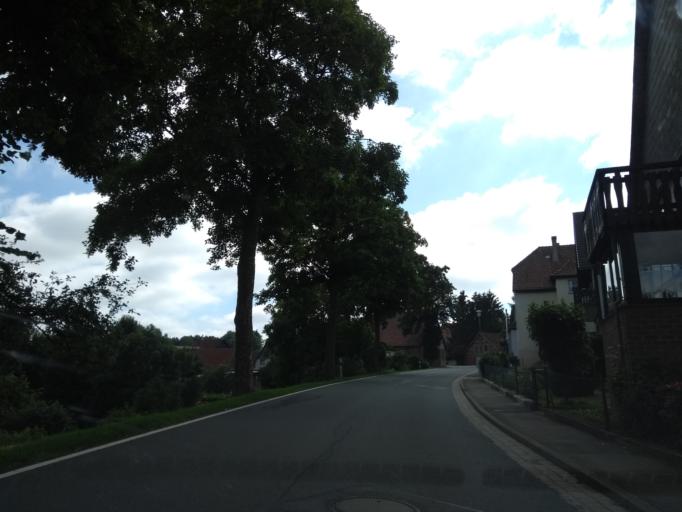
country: DE
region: North Rhine-Westphalia
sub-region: Regierungsbezirk Detmold
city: Lugde
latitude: 51.9594
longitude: 9.3013
